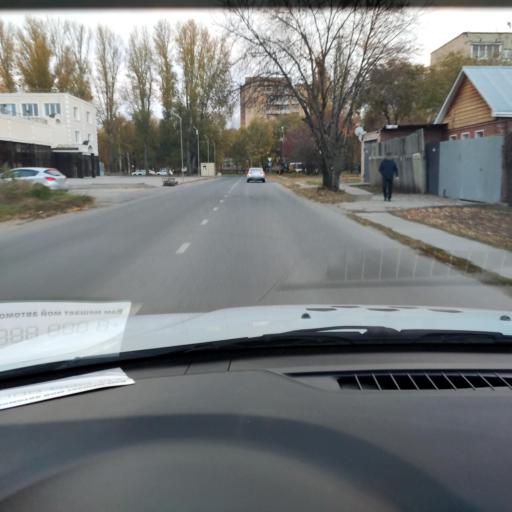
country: RU
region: Samara
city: Tol'yatti
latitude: 53.5338
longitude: 49.4291
